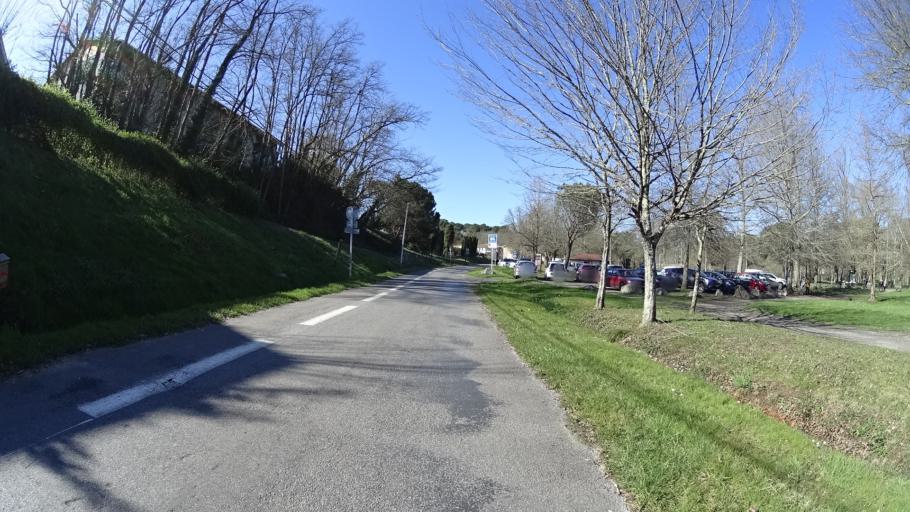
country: FR
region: Aquitaine
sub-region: Departement des Landes
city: Saint-Paul-les-Dax
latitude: 43.7316
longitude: -1.0722
